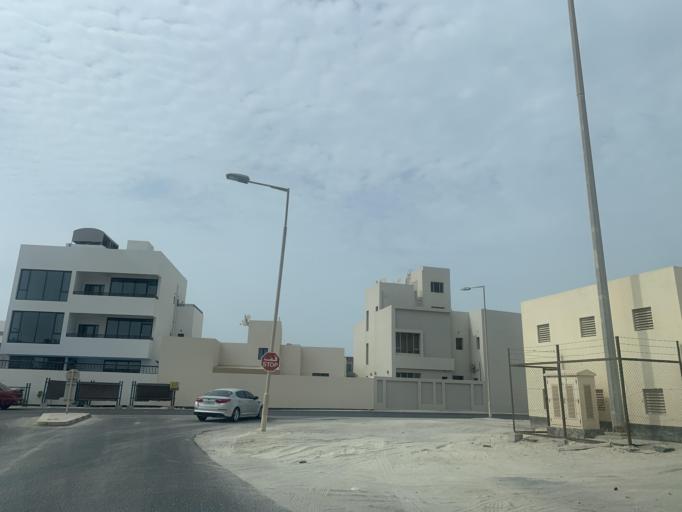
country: BH
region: Muharraq
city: Al Muharraq
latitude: 26.2862
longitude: 50.6344
